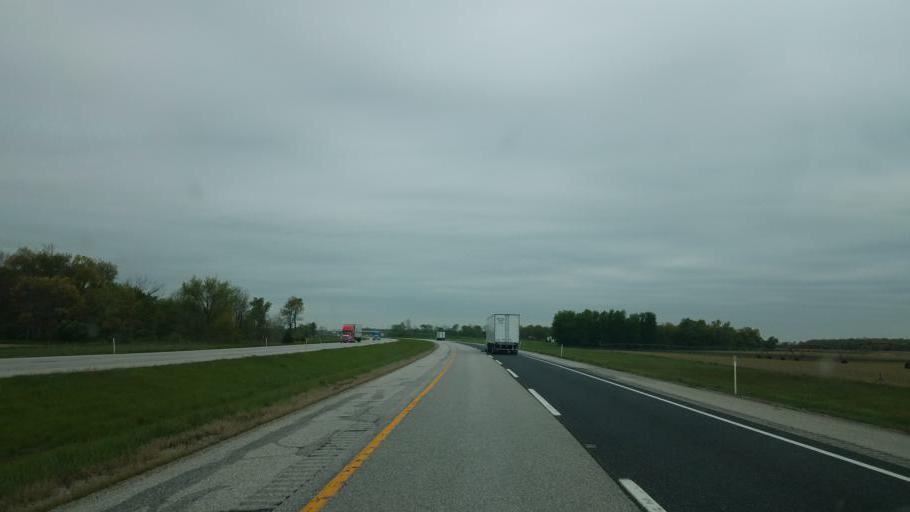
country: US
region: Michigan
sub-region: Saint Joseph County
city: Sturgis
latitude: 41.7535
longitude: -85.4753
